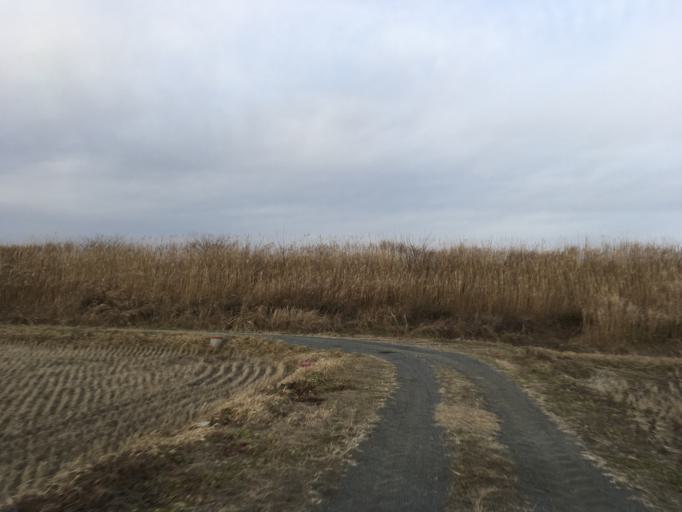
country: JP
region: Miyagi
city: Kogota
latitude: 38.6460
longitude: 141.0698
